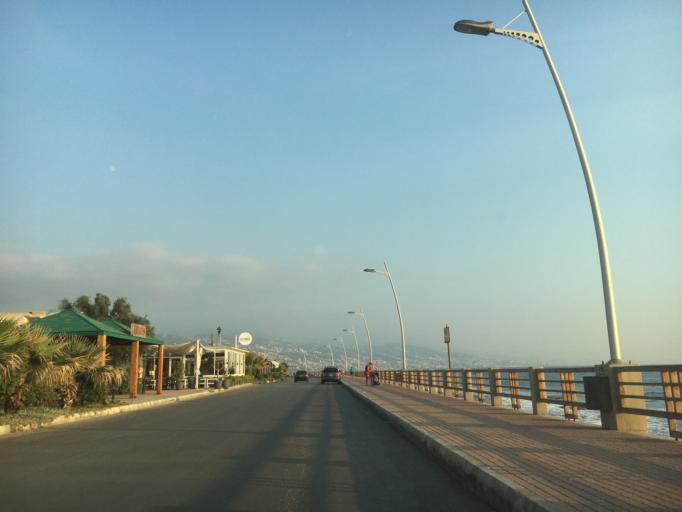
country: LB
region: Mont-Liban
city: Jbail
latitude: 34.1436
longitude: 35.6279
